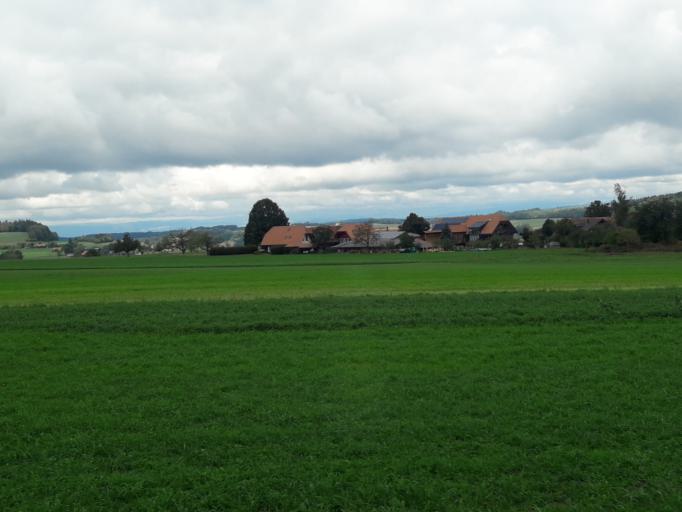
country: CH
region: Fribourg
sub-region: Sense District
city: Flamatt
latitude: 46.8756
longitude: 7.3659
